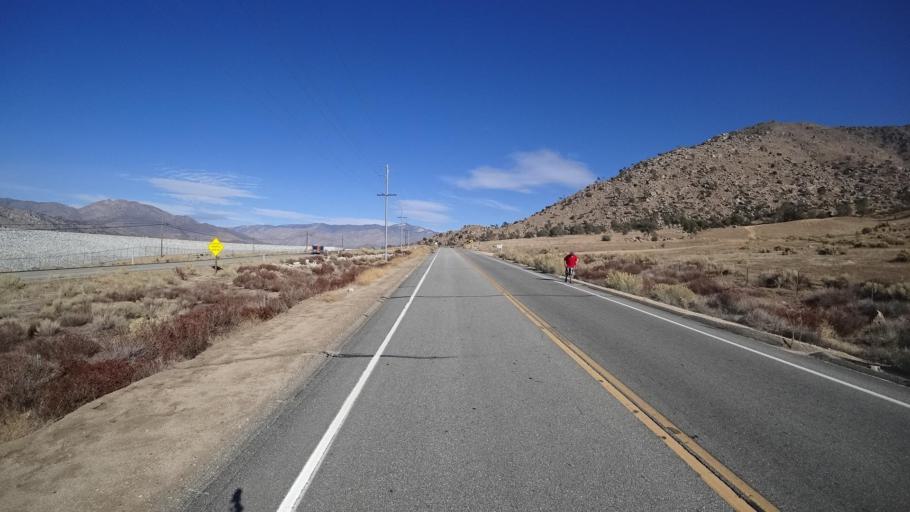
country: US
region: California
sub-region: Kern County
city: Lake Isabella
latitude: 35.6405
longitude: -118.4611
